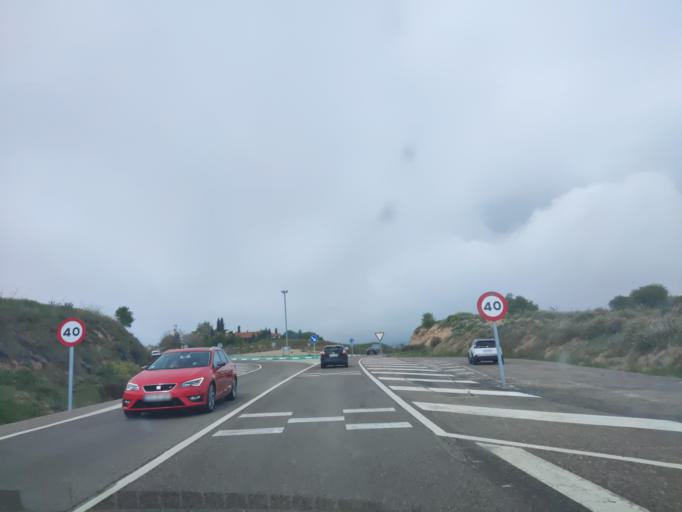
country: ES
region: Castille-La Mancha
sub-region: Province of Toledo
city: Bargas
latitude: 39.9438
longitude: -4.0055
